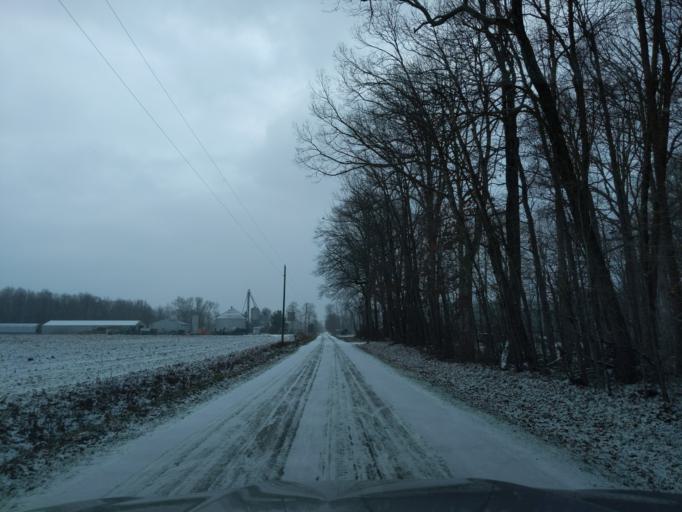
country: US
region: Indiana
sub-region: Decatur County
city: Westport
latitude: 39.2314
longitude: -85.4937
